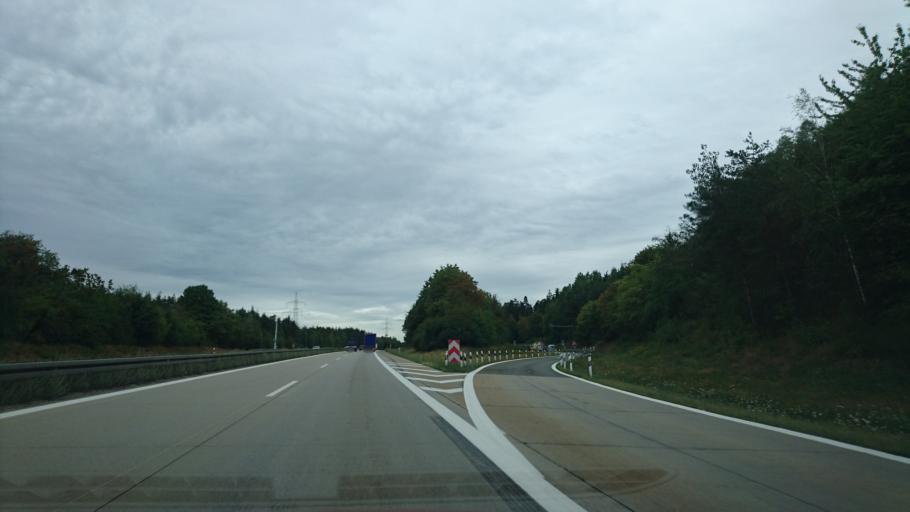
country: DE
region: Bavaria
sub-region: Upper Palatinate
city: Luhe-Wildenau
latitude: 49.5696
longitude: 12.1224
